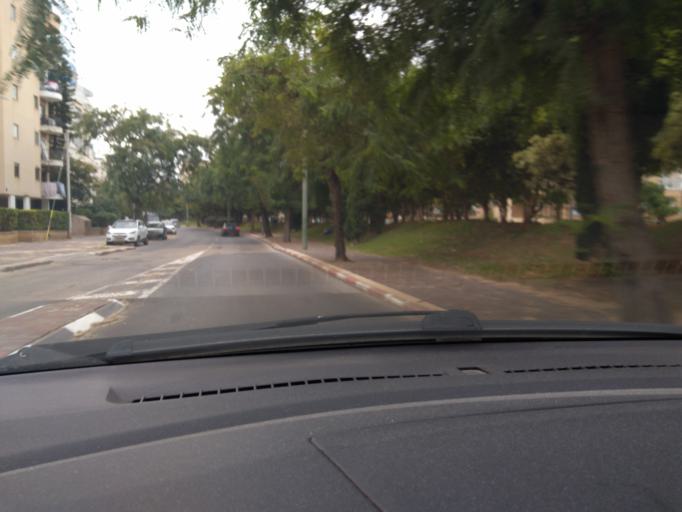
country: IL
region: Central District
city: Netanya
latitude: 32.3422
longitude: 34.8588
